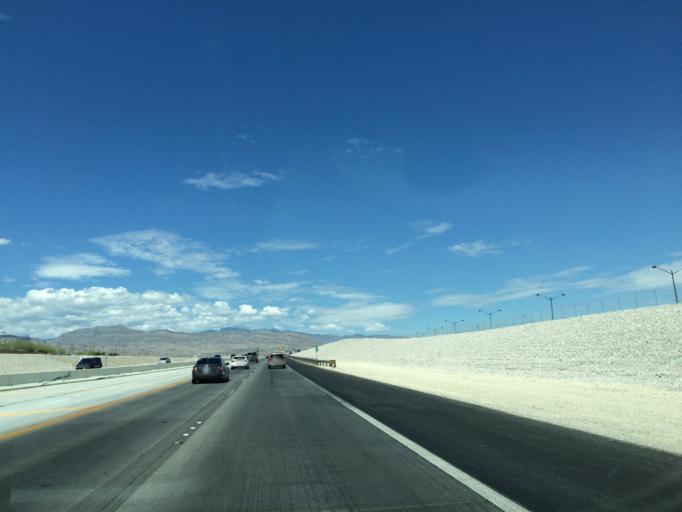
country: US
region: Nevada
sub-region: Clark County
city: Las Vegas
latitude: 36.2764
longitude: -115.2546
